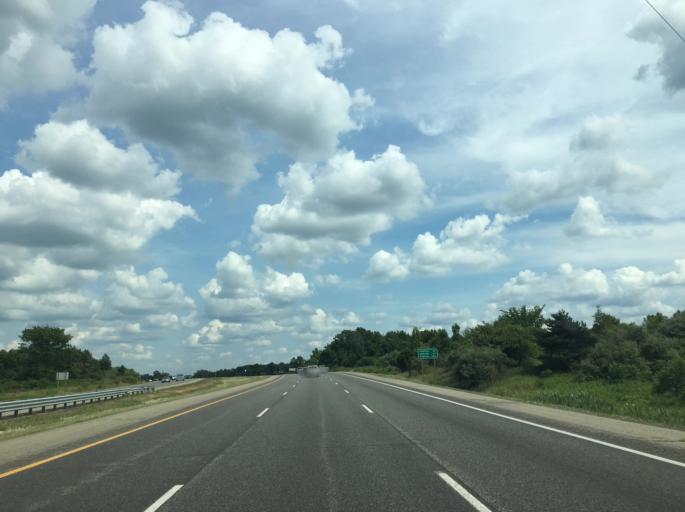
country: US
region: Michigan
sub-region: Genesee County
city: Grand Blanc
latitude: 42.9138
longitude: -83.6713
